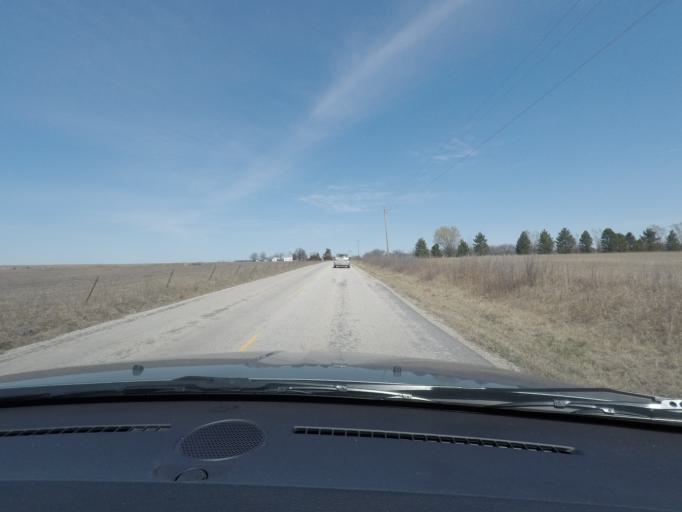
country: US
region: Kansas
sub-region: Lyon County
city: Emporia
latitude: 38.5078
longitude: -96.1705
